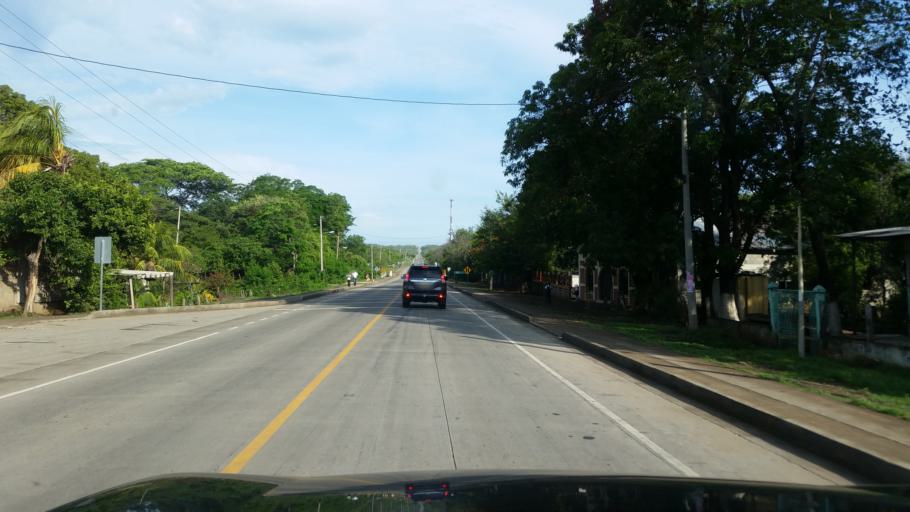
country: NI
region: Managua
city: Carlos Fonseca Amador
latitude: 12.1090
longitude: -86.5944
